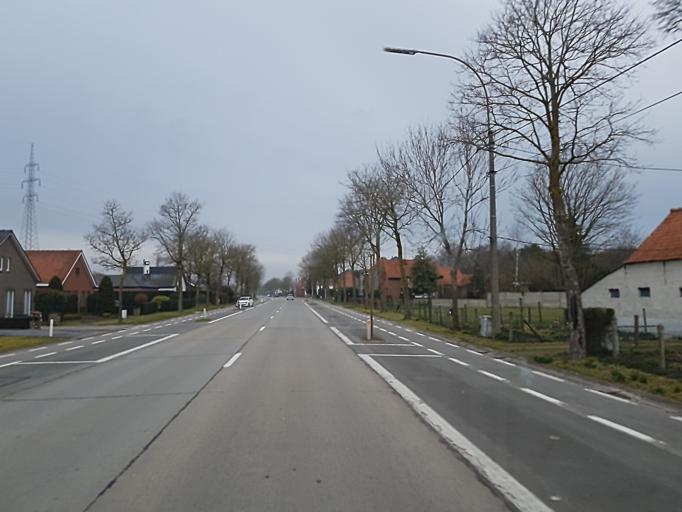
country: BE
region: Flanders
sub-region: Provincie Oost-Vlaanderen
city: Kaprijke
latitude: 51.1879
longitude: 3.6731
